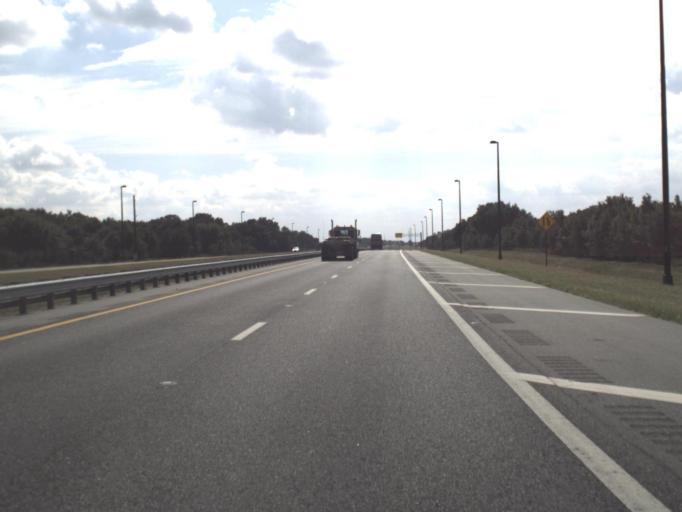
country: US
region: Florida
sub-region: Polk County
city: Polk City
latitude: 28.1294
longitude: -81.8384
